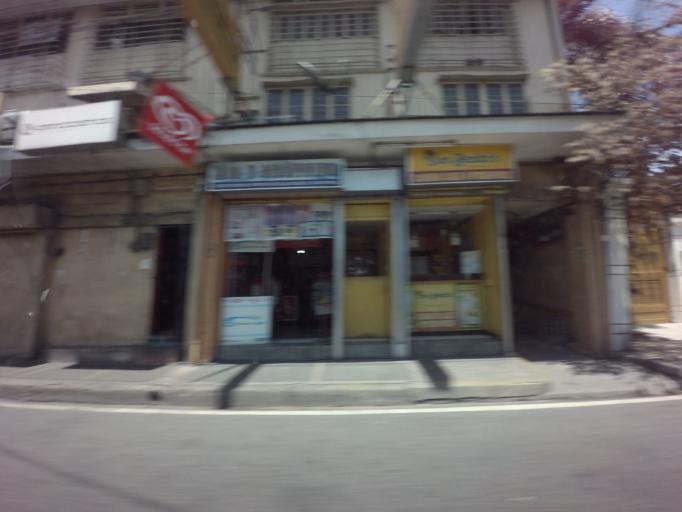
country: PH
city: Sambayanihan People's Village
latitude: 14.5043
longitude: 120.9936
